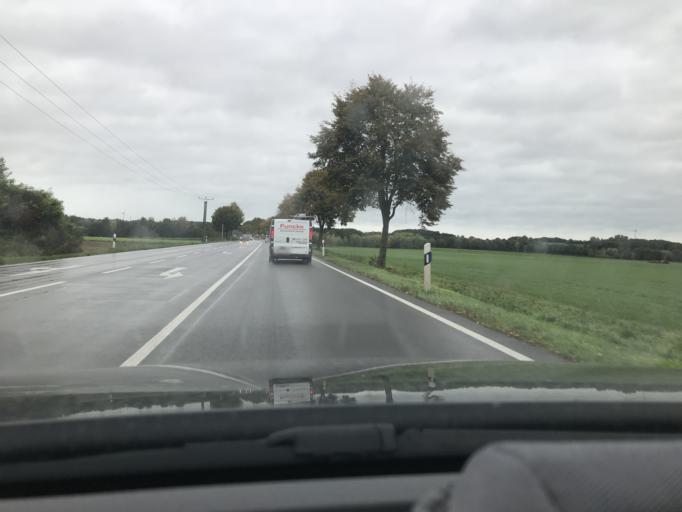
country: DE
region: North Rhine-Westphalia
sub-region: Regierungsbezirk Dusseldorf
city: Nettetal
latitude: 51.3008
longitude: 6.2947
